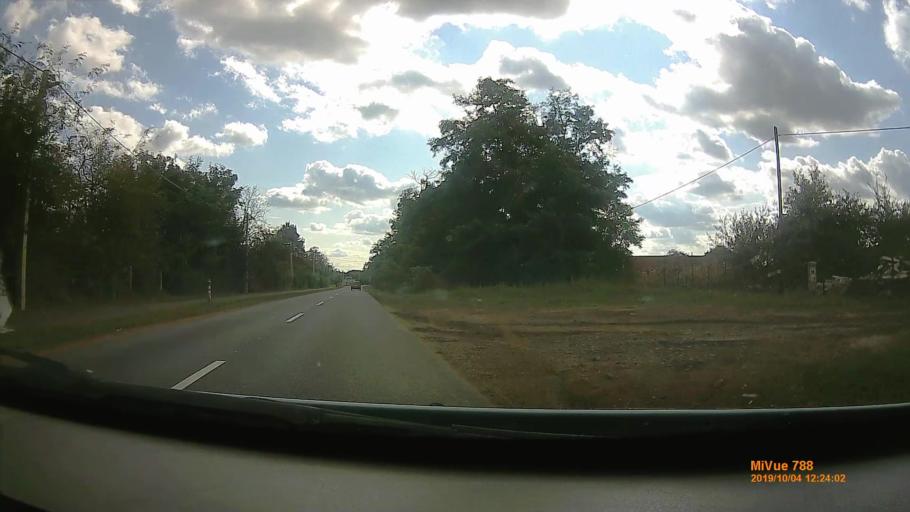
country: HU
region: Szabolcs-Szatmar-Bereg
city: Nyiregyhaza
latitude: 48.0002
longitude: 21.7007
